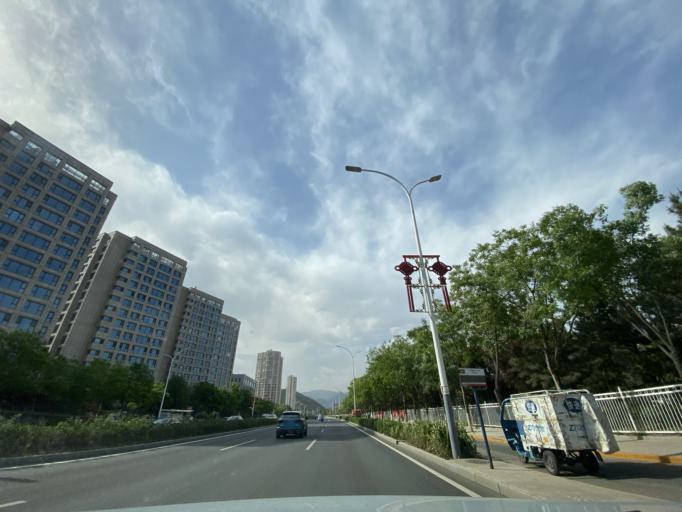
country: CN
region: Beijing
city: Dayu
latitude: 39.9474
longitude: 116.0998
